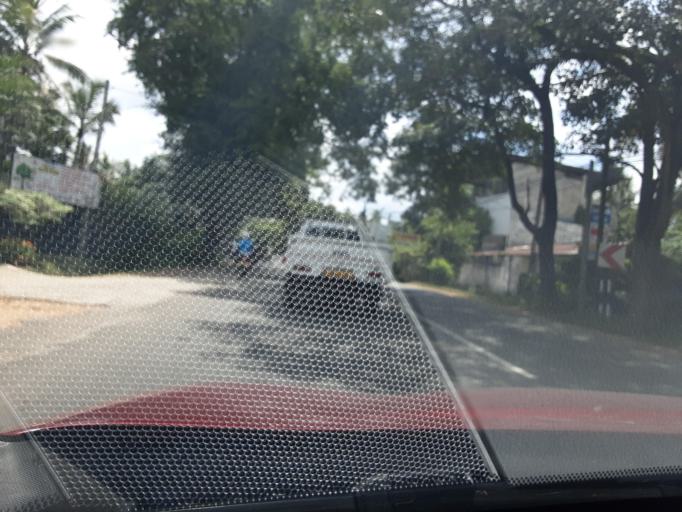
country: LK
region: North Western
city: Kurunegala
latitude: 7.4690
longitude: 80.3138
